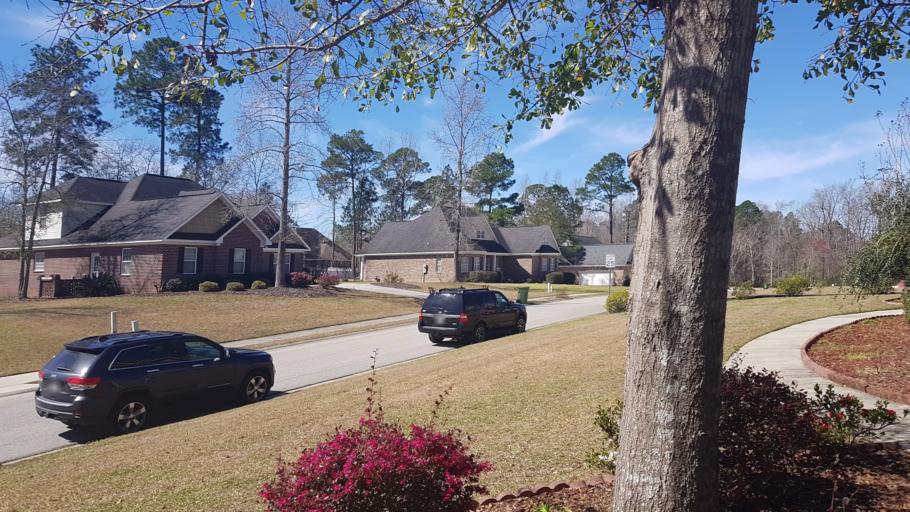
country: US
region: Georgia
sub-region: Bulloch County
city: Statesboro
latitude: 32.4745
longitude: -81.7906
